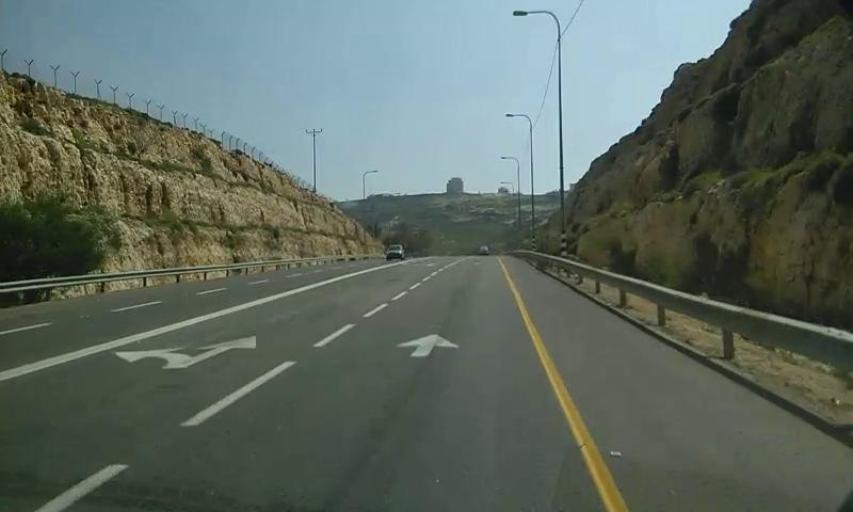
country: PS
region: West Bank
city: Jaba`
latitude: 31.8658
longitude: 35.2590
